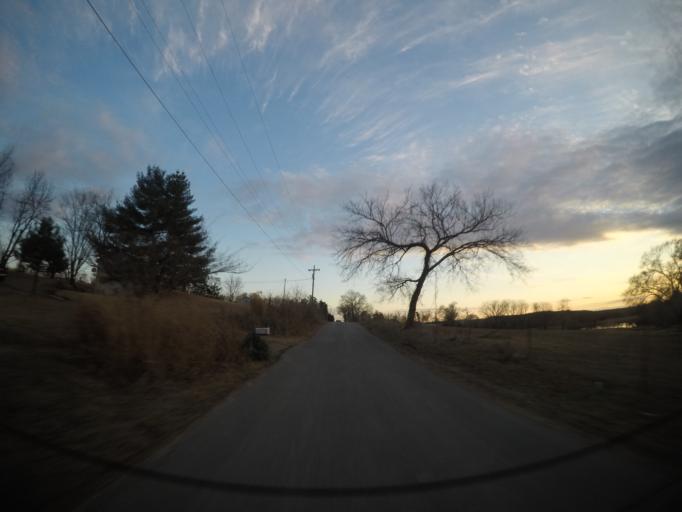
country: US
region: Kansas
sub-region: Wyandotte County
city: Bonner Springs
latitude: 39.0417
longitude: -94.9089
